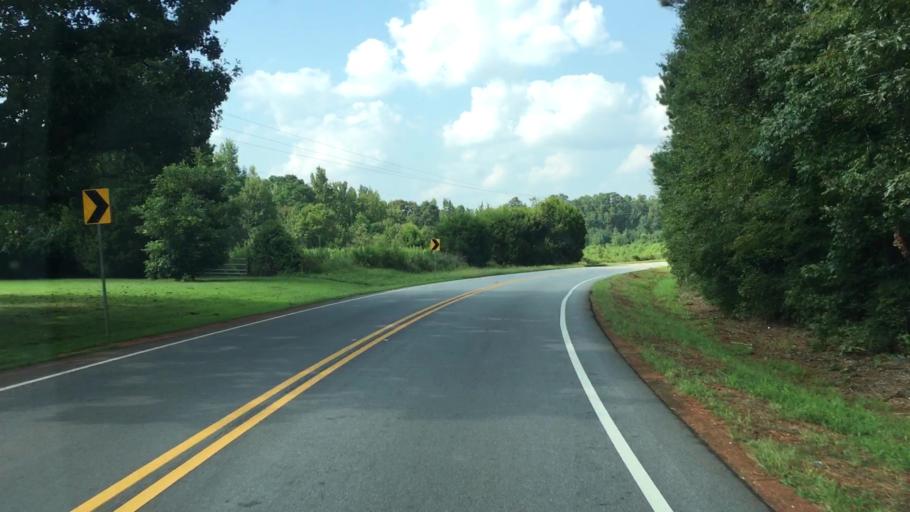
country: US
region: Georgia
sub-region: Jasper County
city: Monticello
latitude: 33.3972
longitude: -83.7597
